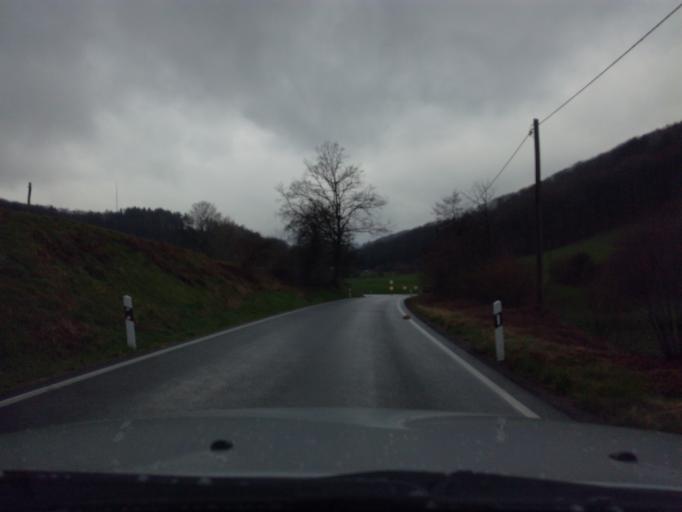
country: DE
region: North Rhine-Westphalia
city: Hattingen
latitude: 51.3562
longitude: 7.1736
